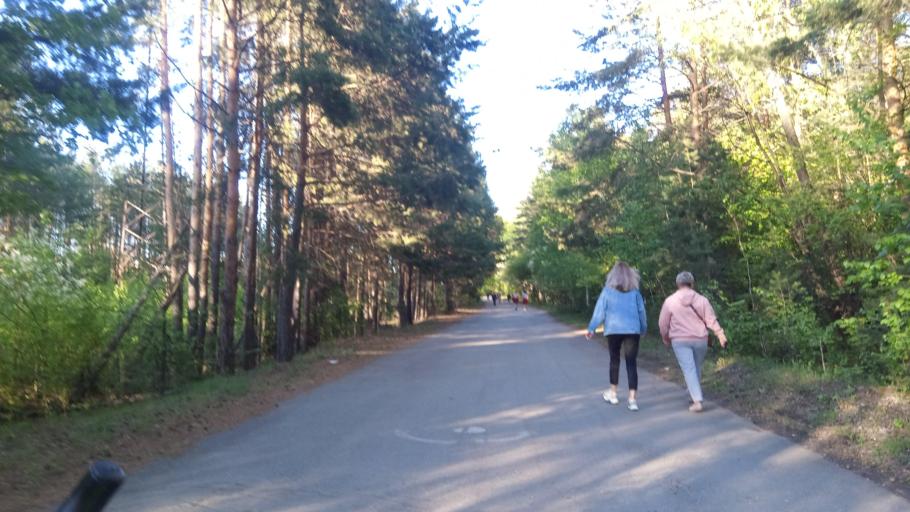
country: RU
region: Chelyabinsk
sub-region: Gorod Chelyabinsk
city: Chelyabinsk
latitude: 55.1522
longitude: 61.3393
